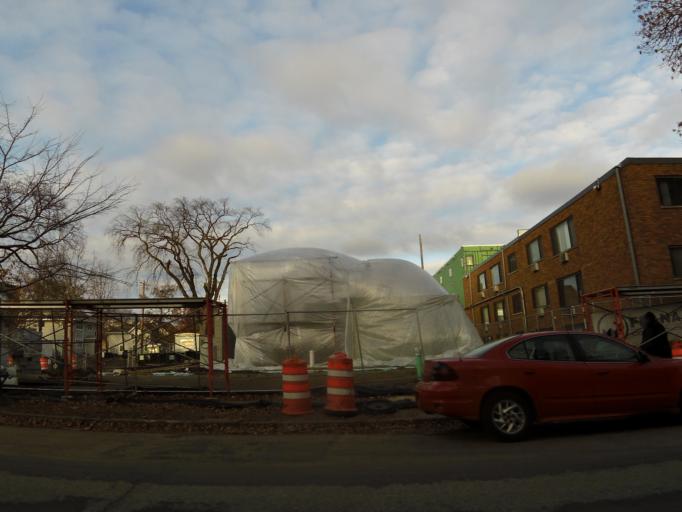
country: US
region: Minnesota
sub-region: Hennepin County
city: Minneapolis
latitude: 44.9851
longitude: -93.2506
